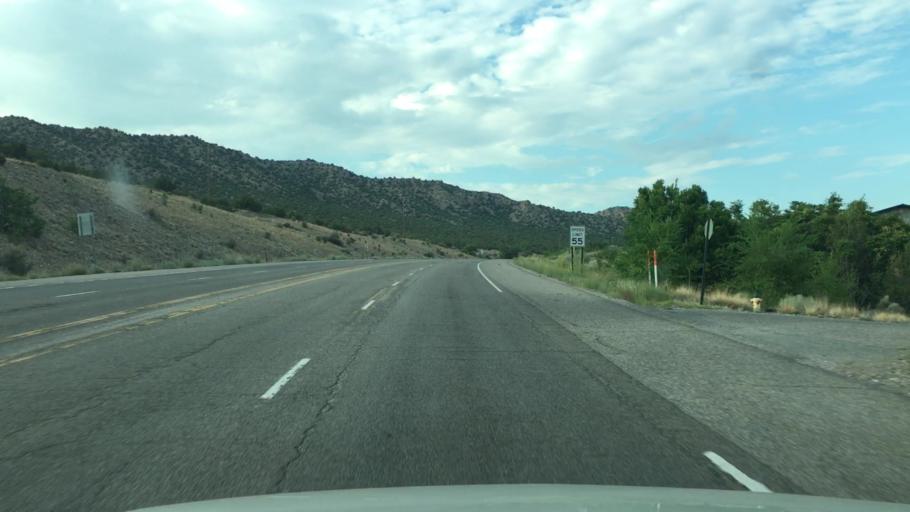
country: US
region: New Mexico
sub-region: Rio Arriba County
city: Ohkay Owingeh
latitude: 36.1619
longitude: -105.9672
